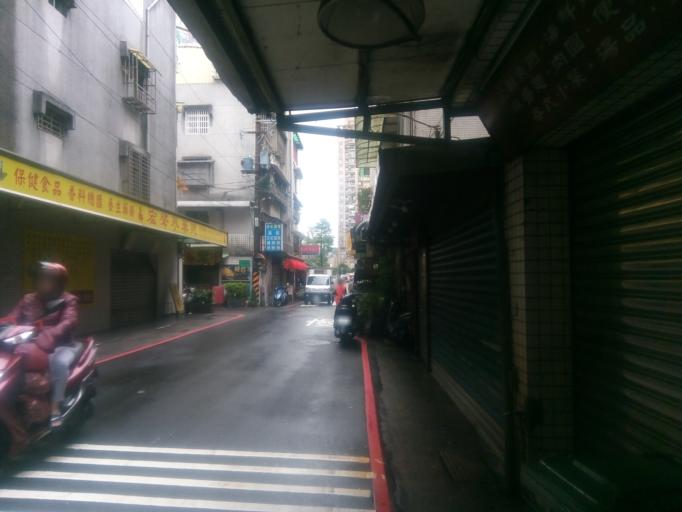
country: TW
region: Taiwan
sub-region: Keelung
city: Keelung
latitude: 25.0713
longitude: 121.6624
